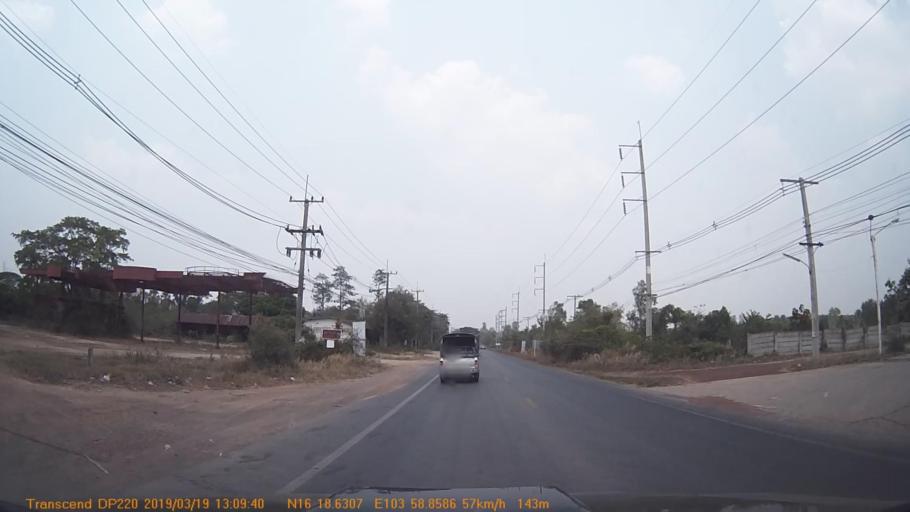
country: TH
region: Roi Et
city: Waeng
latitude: 16.3107
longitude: 103.9810
